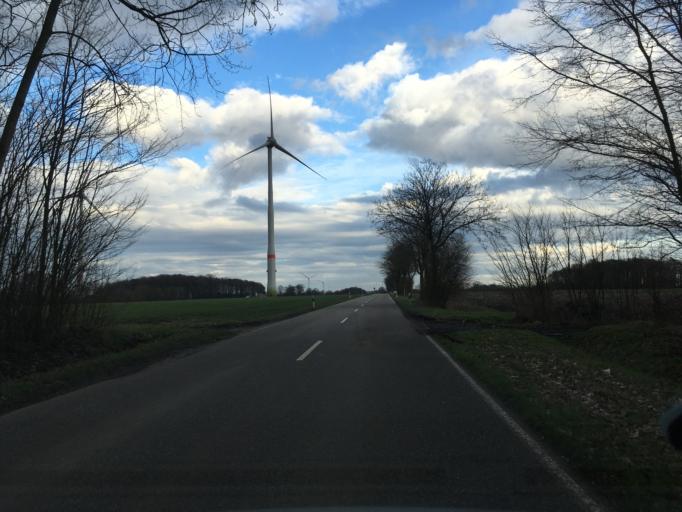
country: DE
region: North Rhine-Westphalia
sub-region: Regierungsbezirk Munster
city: Schoppingen
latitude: 52.0602
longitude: 7.1717
